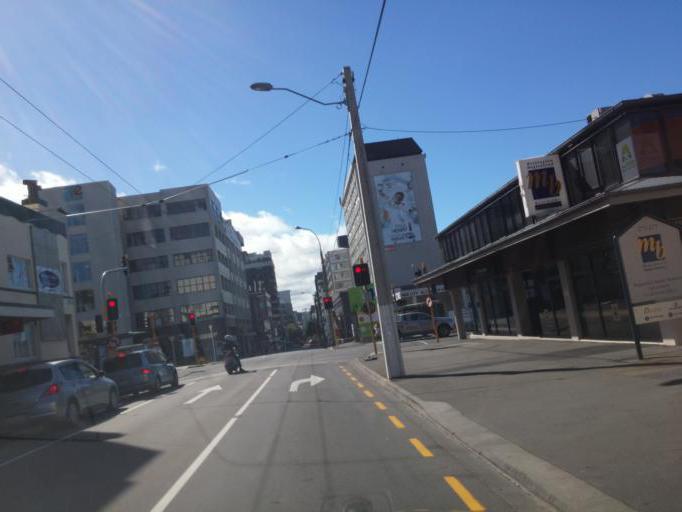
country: NZ
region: Wellington
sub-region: Wellington City
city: Wellington
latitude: -41.2942
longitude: 174.7719
